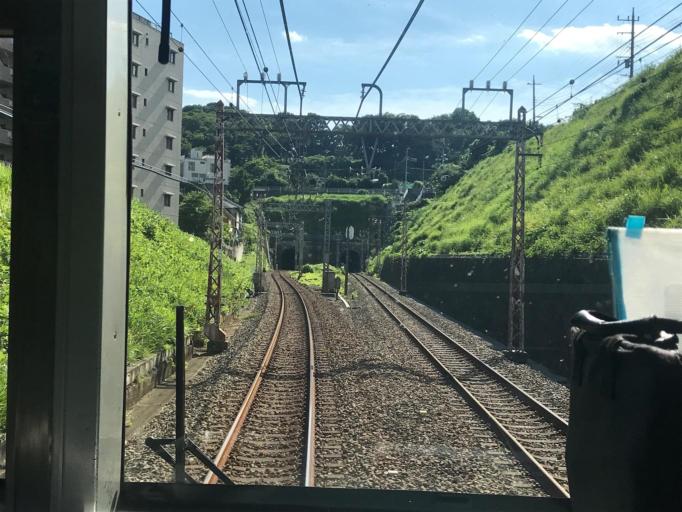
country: JP
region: Kanagawa
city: Hadano
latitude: 35.3657
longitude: 139.2545
